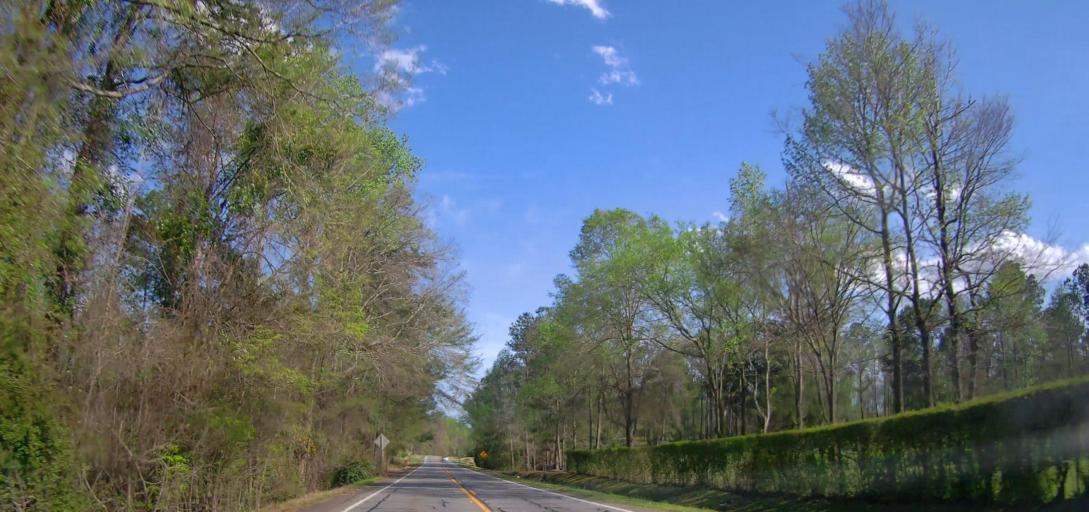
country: US
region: Georgia
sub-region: Baldwin County
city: Hardwick
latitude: 33.0902
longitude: -83.1766
